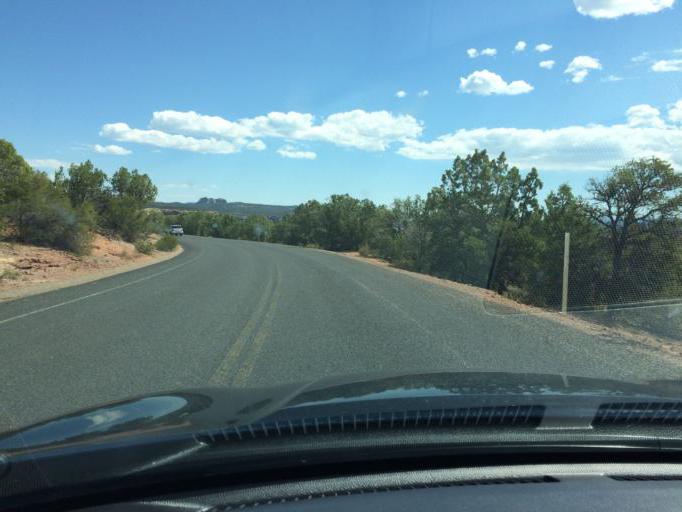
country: US
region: Arizona
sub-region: Apache County
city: Chinle
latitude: 36.1013
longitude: -109.3582
